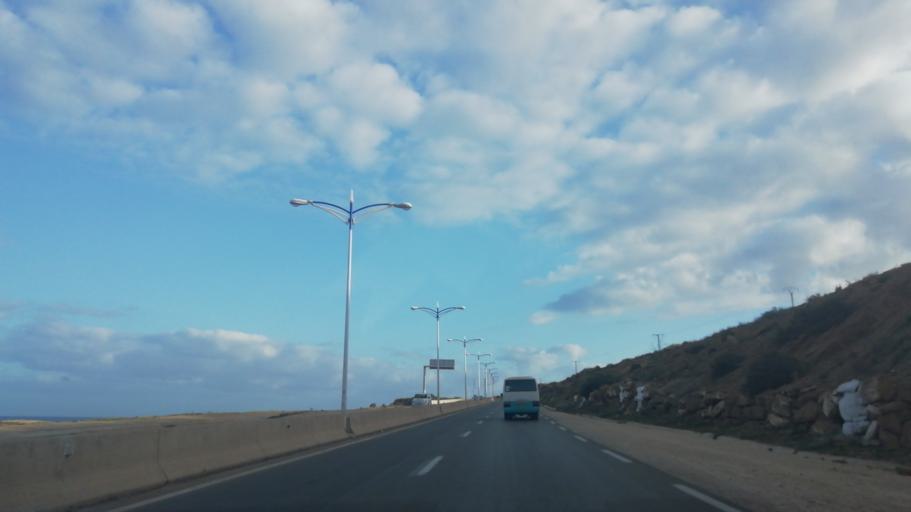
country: DZ
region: Mostaganem
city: Mostaganem
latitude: 36.0386
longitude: 0.1436
